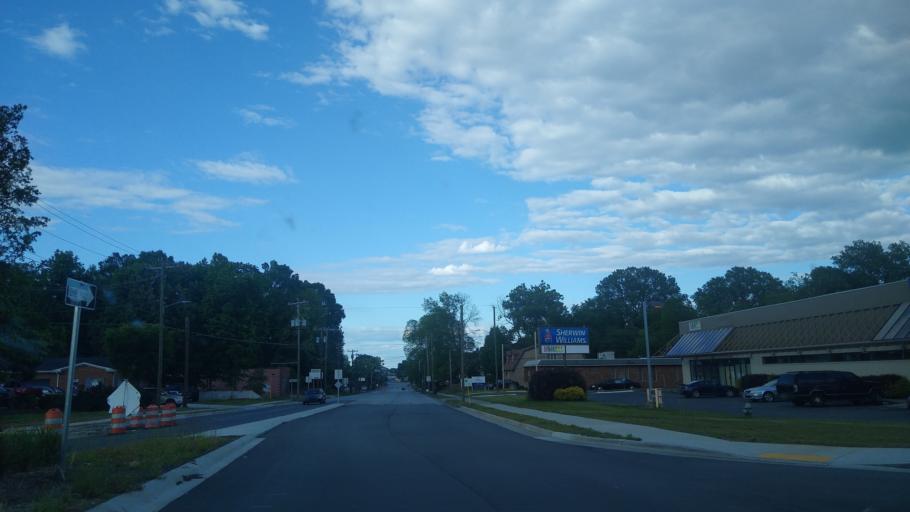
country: US
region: North Carolina
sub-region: Guilford County
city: Greensboro
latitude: 36.0787
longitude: -79.7835
